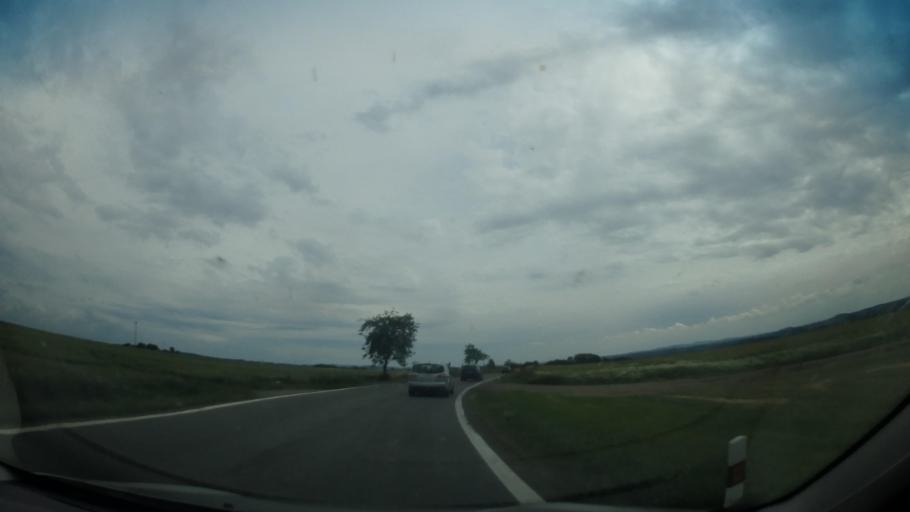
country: CZ
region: Vysocina
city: Bystrice nad Pernstejnem
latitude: 49.5048
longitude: 16.1703
